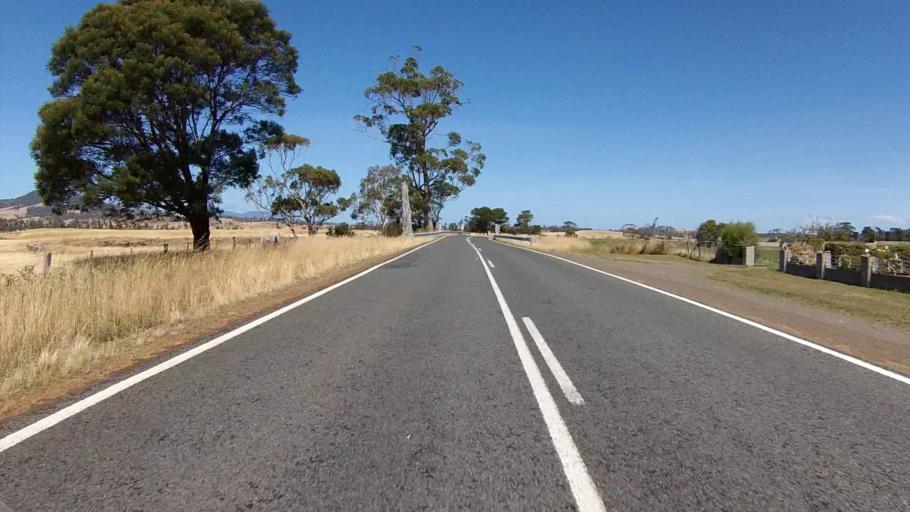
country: AU
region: Tasmania
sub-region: Sorell
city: Sorell
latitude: -42.4454
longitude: 147.9286
